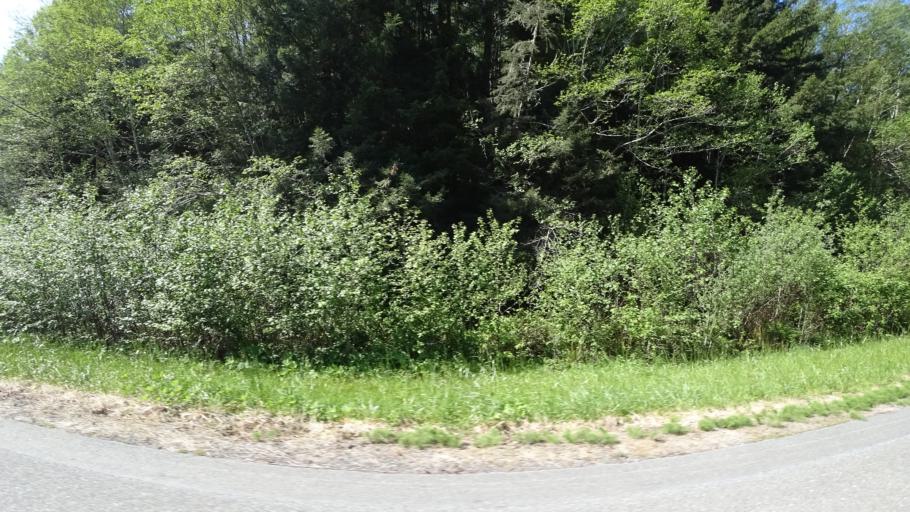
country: US
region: California
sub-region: Del Norte County
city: Bertsch-Oceanview
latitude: 41.4657
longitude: -124.0388
